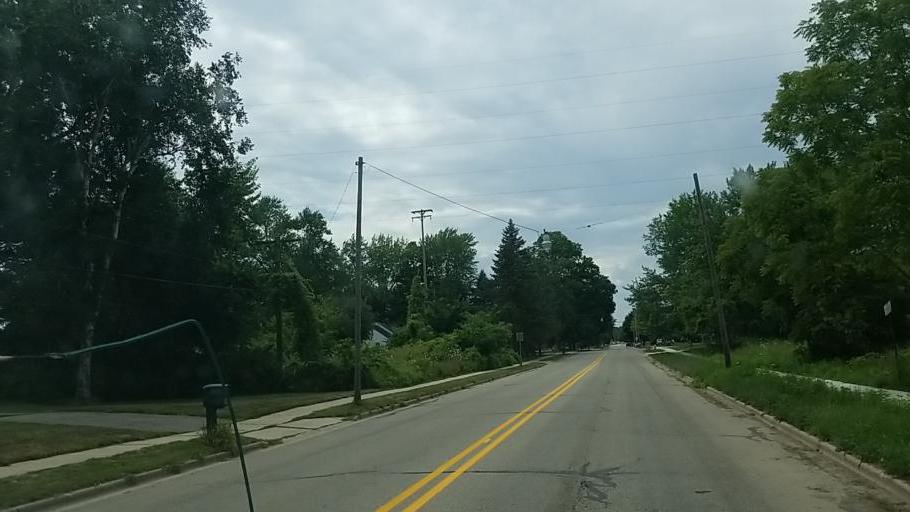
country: US
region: Michigan
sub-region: Kent County
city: Walker
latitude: 43.0012
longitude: -85.7568
